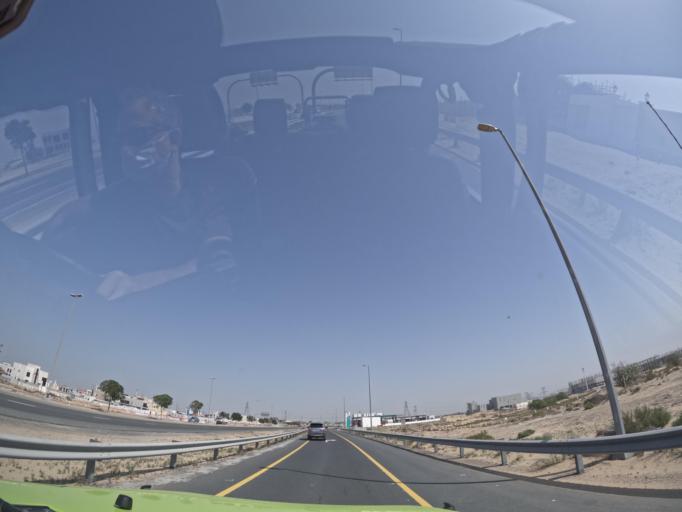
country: AE
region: Ash Shariqah
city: Sharjah
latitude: 25.1570
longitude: 55.3632
